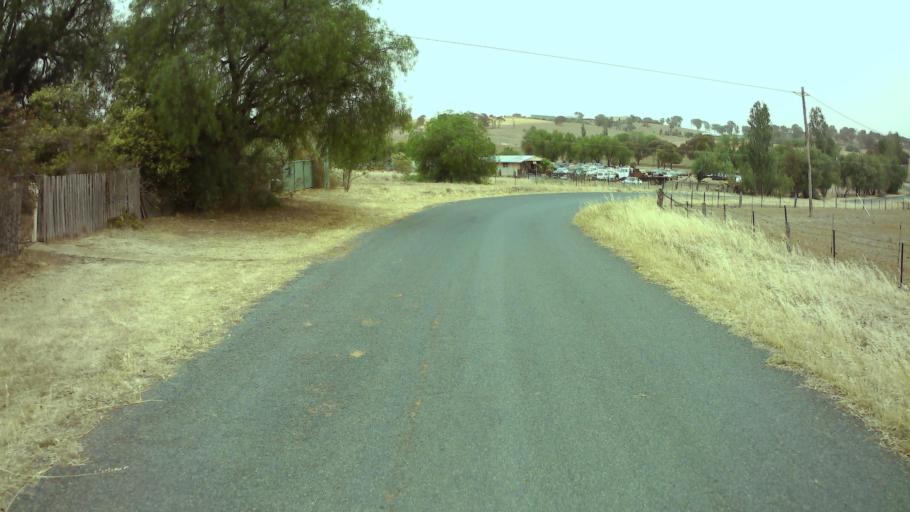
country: AU
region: New South Wales
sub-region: Weddin
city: Grenfell
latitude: -33.9053
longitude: 148.1698
